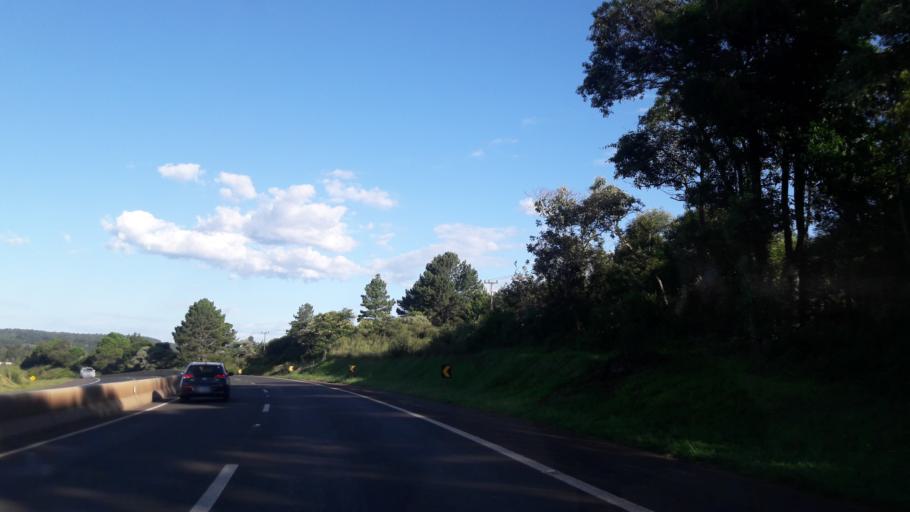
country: BR
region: Parana
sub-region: Guarapuava
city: Guarapuava
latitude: -25.3532
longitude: -51.3737
